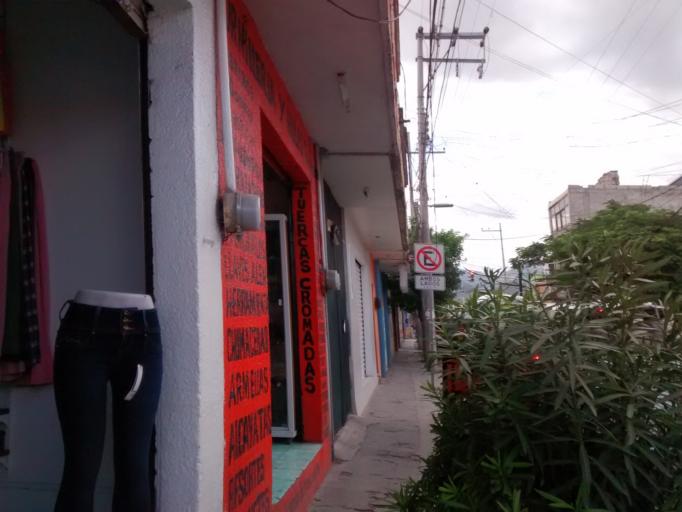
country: MX
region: Puebla
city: Tehuacan
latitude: 18.4622
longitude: -97.3872
